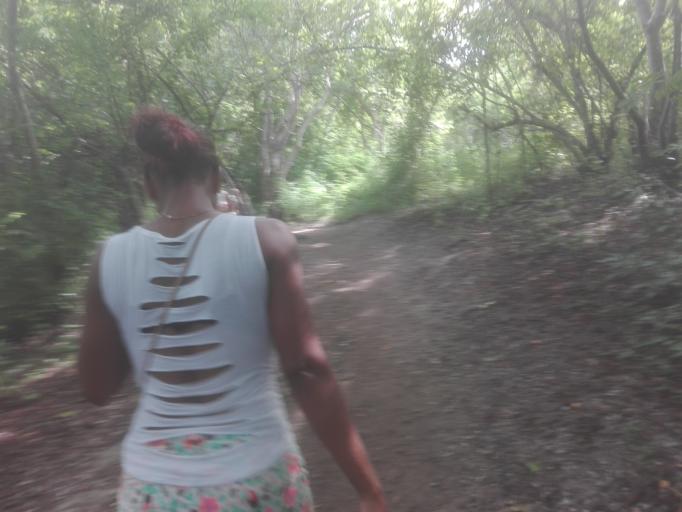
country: CO
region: Bolivar
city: Turbana
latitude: 10.1800
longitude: -75.7338
